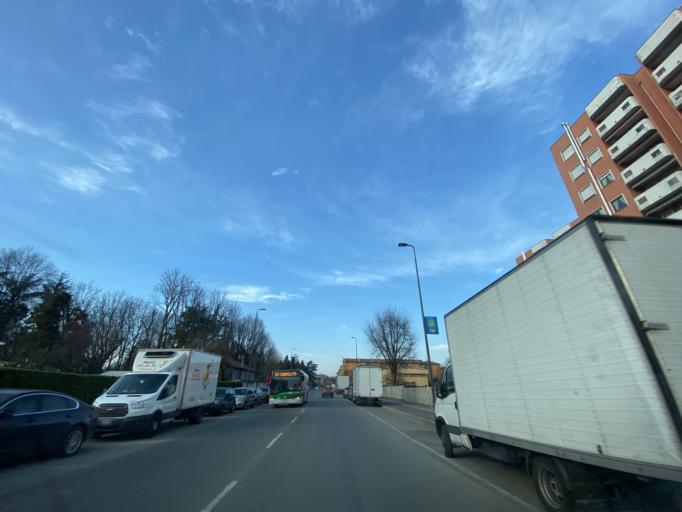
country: IT
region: Lombardy
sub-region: Citta metropolitana di Milano
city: Novate Milanese
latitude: 45.5150
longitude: 9.1363
